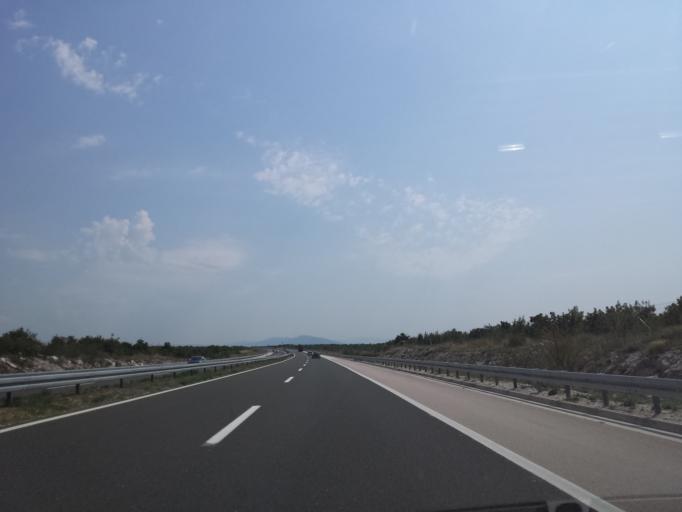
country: HR
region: Sibensko-Kniniska
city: Zaton
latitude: 43.8709
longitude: 15.8081
